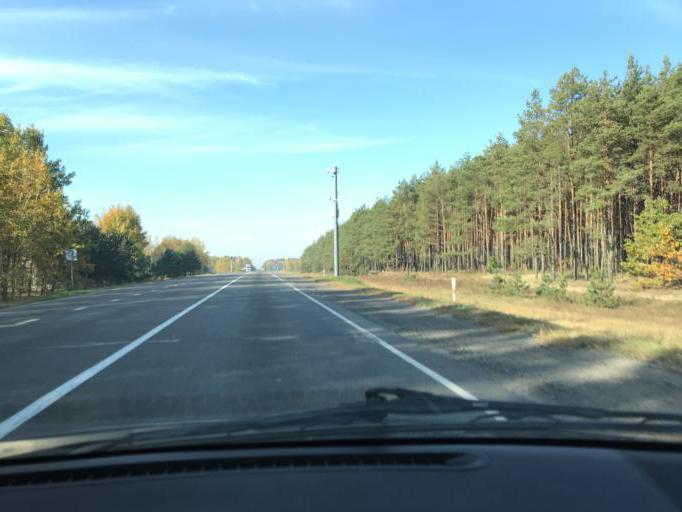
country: BY
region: Brest
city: Davyd-Haradok
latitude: 52.2445
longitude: 27.1453
